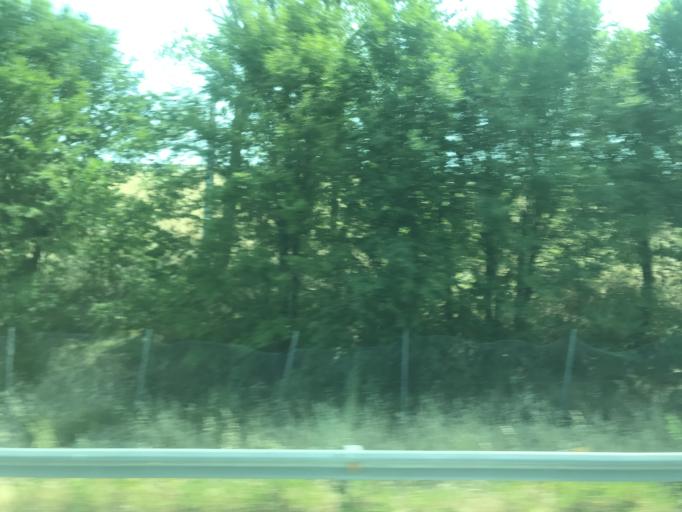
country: ES
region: Madrid
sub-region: Provincia de Madrid
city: Pedrezuela
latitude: 40.7646
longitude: -3.6040
